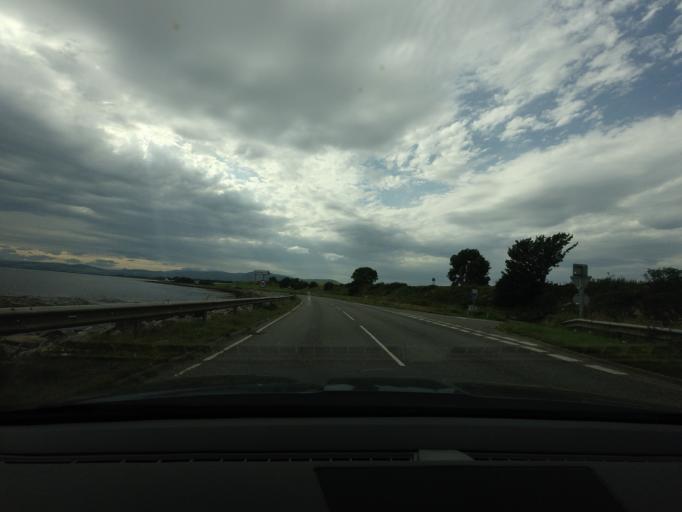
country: GB
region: Scotland
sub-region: Highland
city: Invergordon
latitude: 57.6926
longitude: -4.2019
